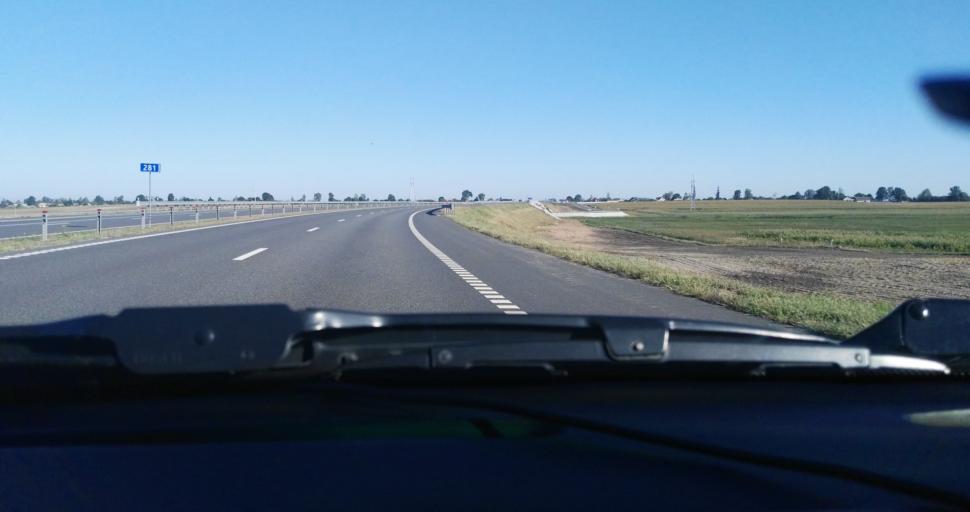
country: BY
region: Gomel
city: Buda-Kashalyova
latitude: 52.5102
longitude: 30.6316
